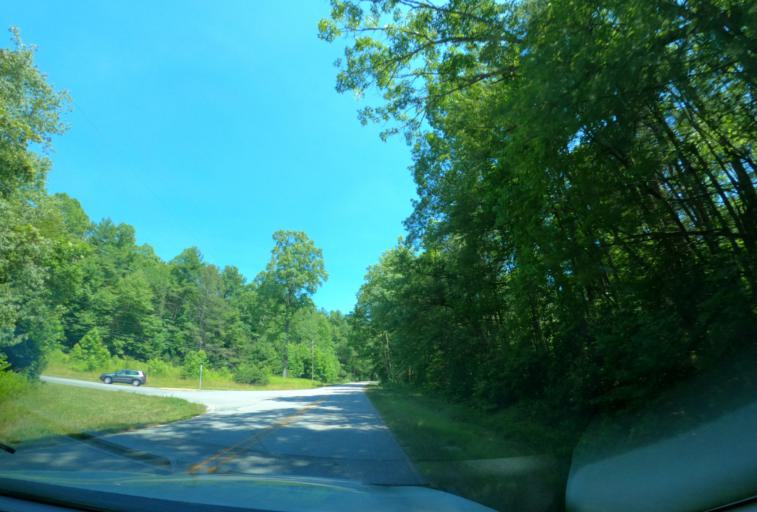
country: US
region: North Carolina
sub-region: Transylvania County
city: Brevard
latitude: 35.1824
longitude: -82.6421
